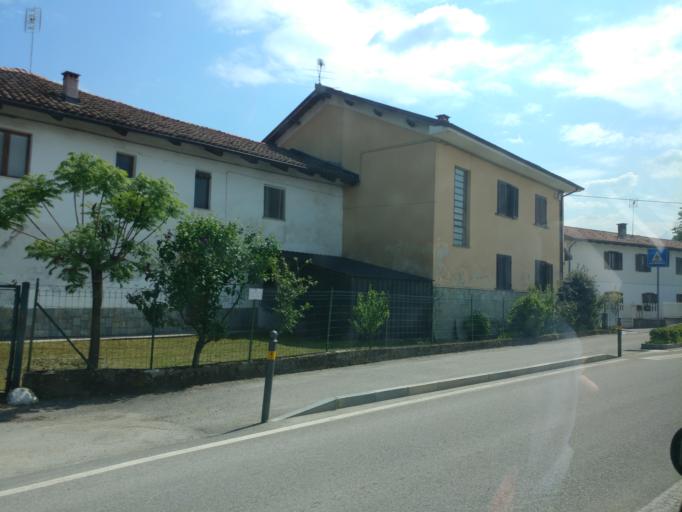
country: IT
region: Piedmont
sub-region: Provincia di Cuneo
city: Saluzzo
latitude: 44.6430
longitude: 7.4647
